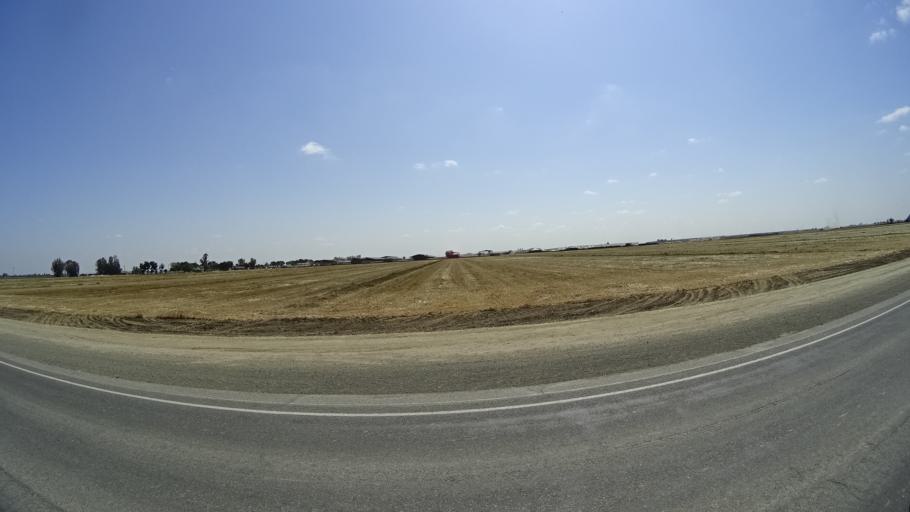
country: US
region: California
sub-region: Kings County
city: Home Garden
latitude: 36.2662
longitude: -119.6370
